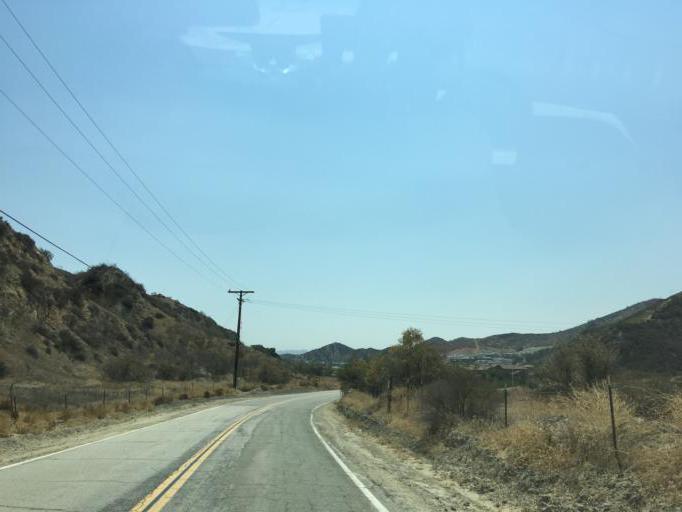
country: US
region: California
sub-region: Los Angeles County
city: Santa Clarita
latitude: 34.3791
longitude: -118.5965
